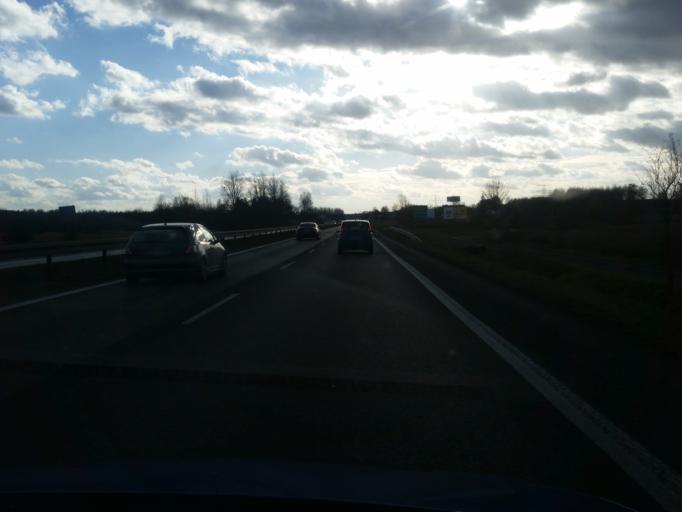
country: PL
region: Silesian Voivodeship
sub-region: Powiat czestochowski
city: Kamienica Polska
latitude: 50.6831
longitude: 19.1299
